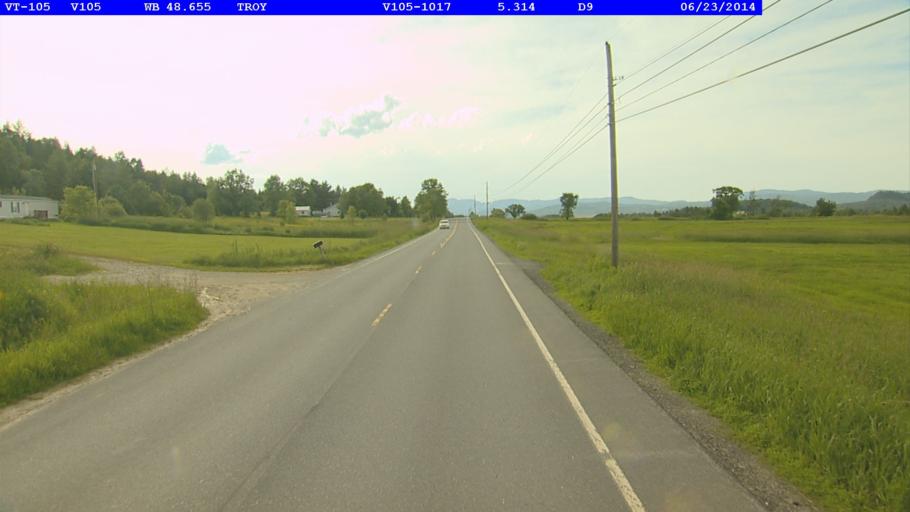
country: US
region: Vermont
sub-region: Orleans County
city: Newport
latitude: 44.9820
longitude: -72.3553
